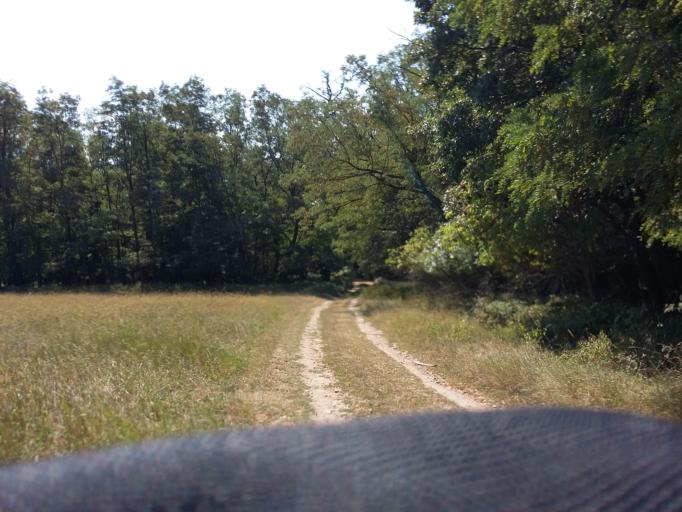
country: SK
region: Bratislavsky
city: Stupava
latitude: 48.3116
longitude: 17.0351
